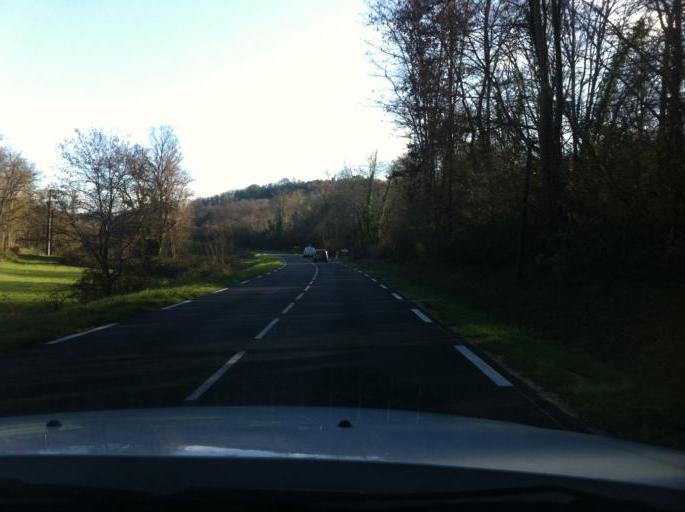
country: FR
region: Aquitaine
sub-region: Departement de la Dordogne
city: Rouffignac-Saint-Cernin-de-Reilhac
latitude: 45.0375
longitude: 0.8945
